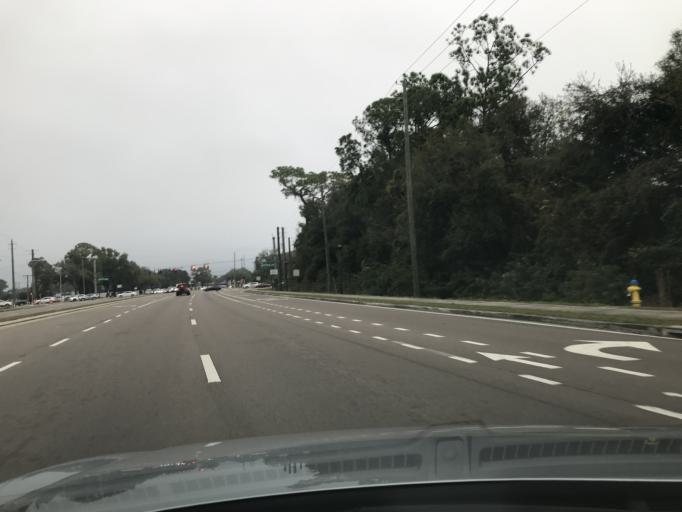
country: US
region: Florida
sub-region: Pinellas County
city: Oldsmar
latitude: 28.0548
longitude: -82.6487
